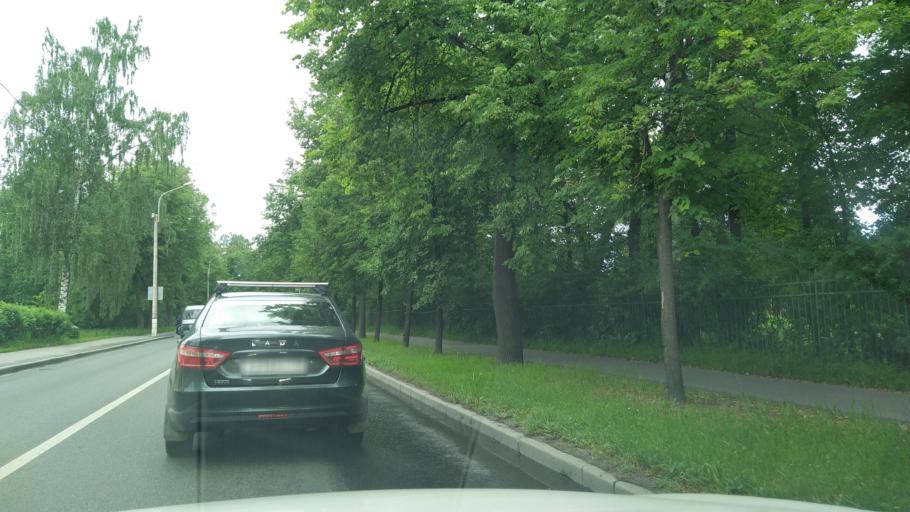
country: RU
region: St.-Petersburg
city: Pavlovsk
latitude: 59.6852
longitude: 30.4472
